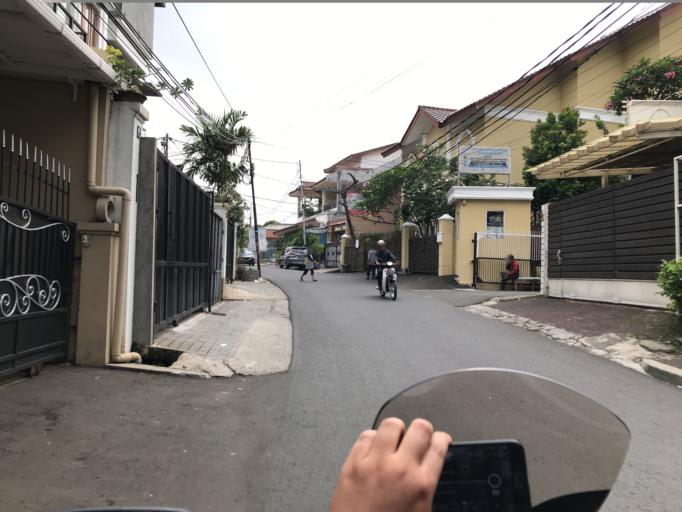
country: ID
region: Jakarta Raya
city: Jakarta
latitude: -6.2378
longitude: 106.8535
